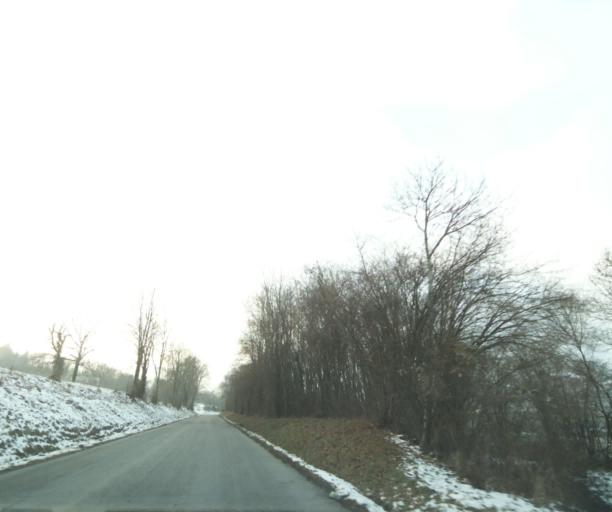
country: FR
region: Rhone-Alpes
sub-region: Departement de la Haute-Savoie
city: Arthaz-Pont-Notre-Dame
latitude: 46.1568
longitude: 6.2428
